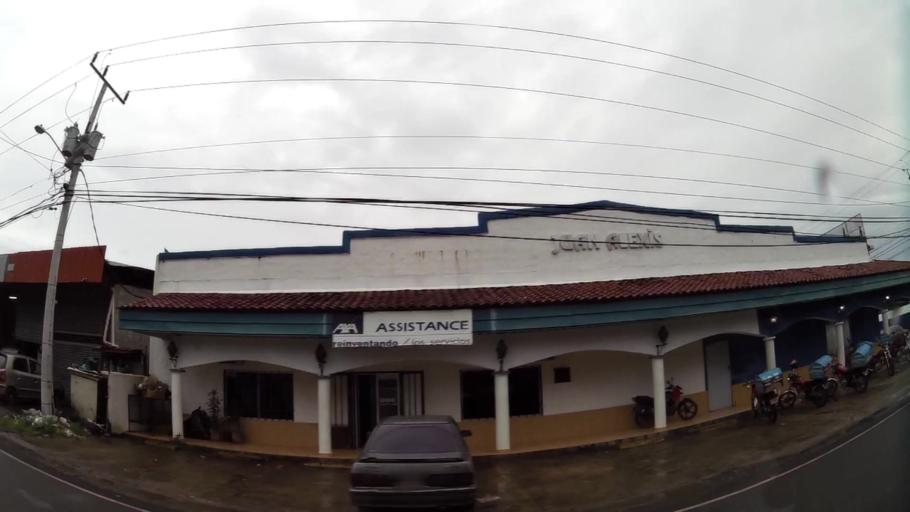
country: PA
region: Veraguas
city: Santiago de Veraguas
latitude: 8.1090
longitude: -80.9739
